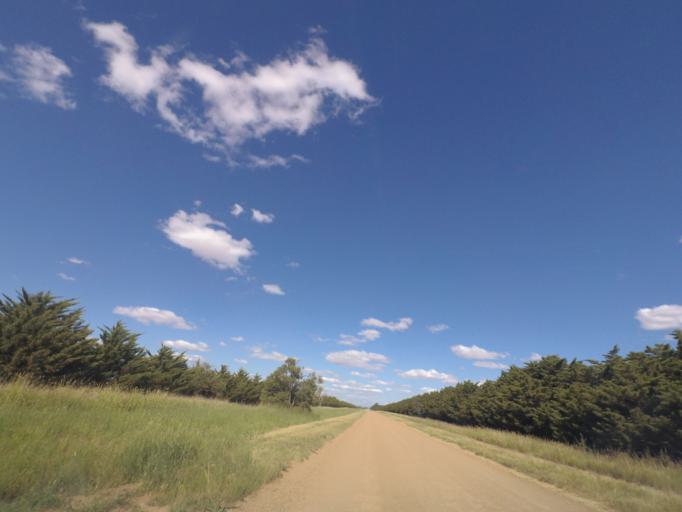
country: AU
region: Victoria
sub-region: Hume
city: Sunbury
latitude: -37.4586
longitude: 144.7887
